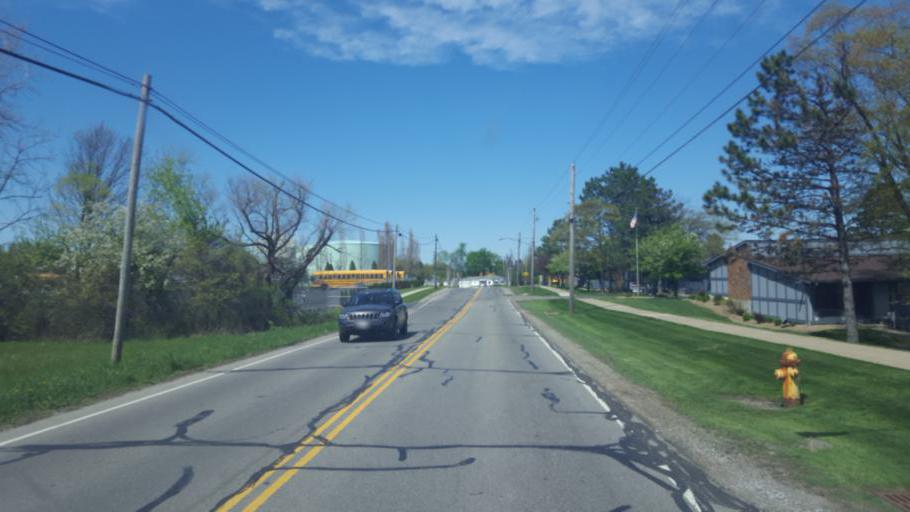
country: US
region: Ohio
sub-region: Ashland County
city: Ashland
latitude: 40.8539
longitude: -82.3328
